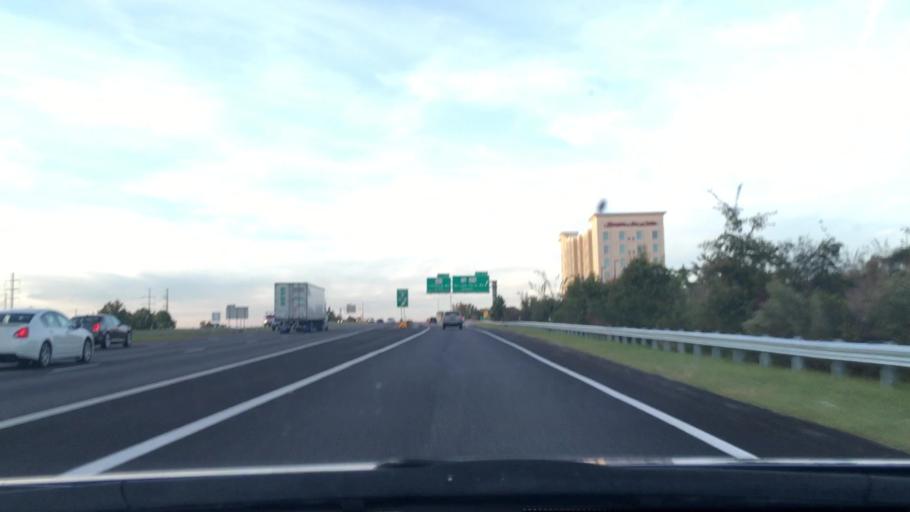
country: US
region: South Carolina
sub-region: Richland County
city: Forest Acres
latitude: 33.9680
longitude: -80.9534
